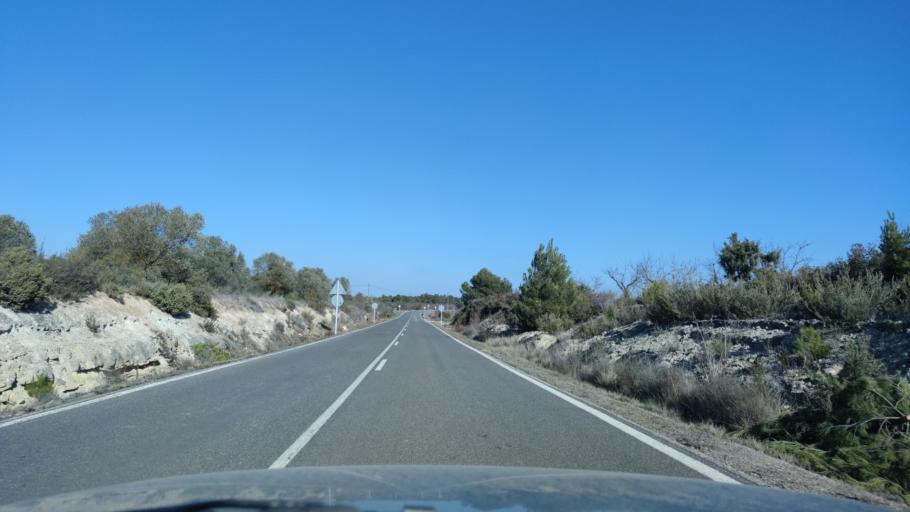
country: ES
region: Catalonia
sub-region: Provincia de Lleida
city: Maials
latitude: 41.3394
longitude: 0.4629
